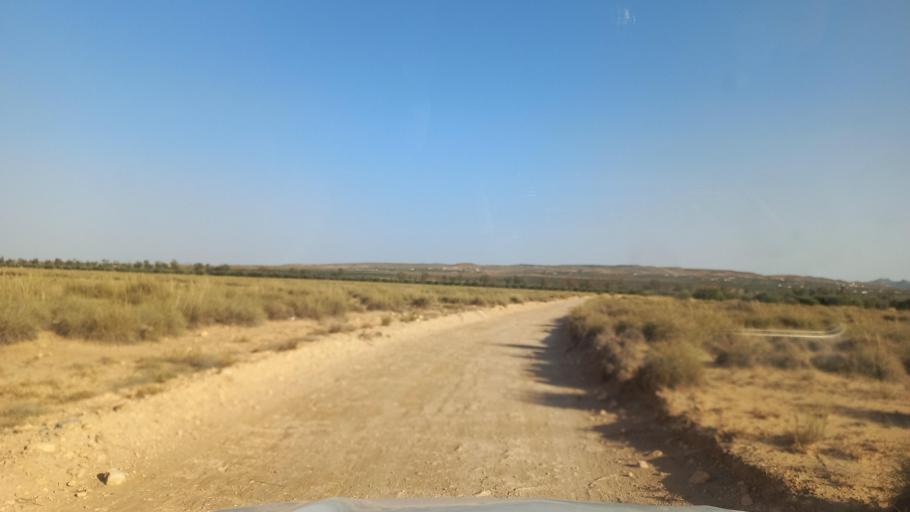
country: TN
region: Al Qasrayn
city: Kasserine
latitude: 35.2304
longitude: 8.9409
